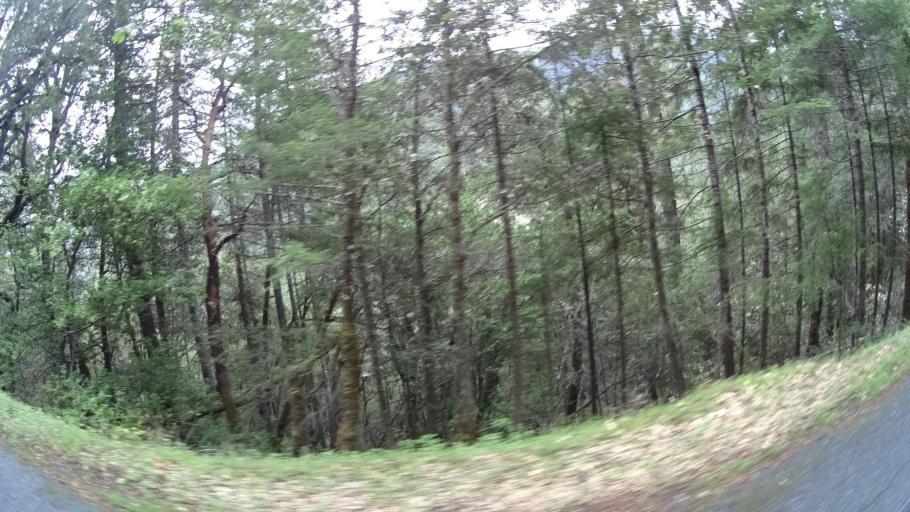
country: US
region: California
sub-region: Humboldt County
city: Willow Creek
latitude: 41.3516
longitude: -123.5119
